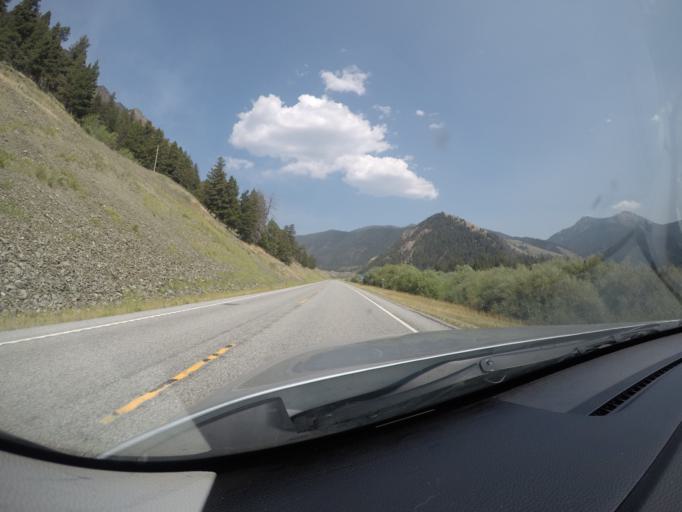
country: US
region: Montana
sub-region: Gallatin County
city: West Yellowstone
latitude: 44.8264
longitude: -111.4503
